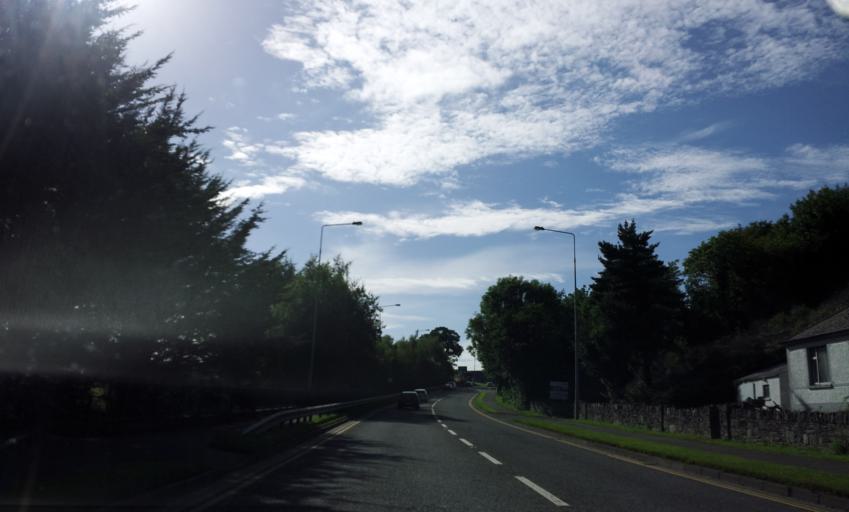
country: IE
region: Munster
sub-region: Ciarrai
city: Cill Airne
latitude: 52.0588
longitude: -9.4765
